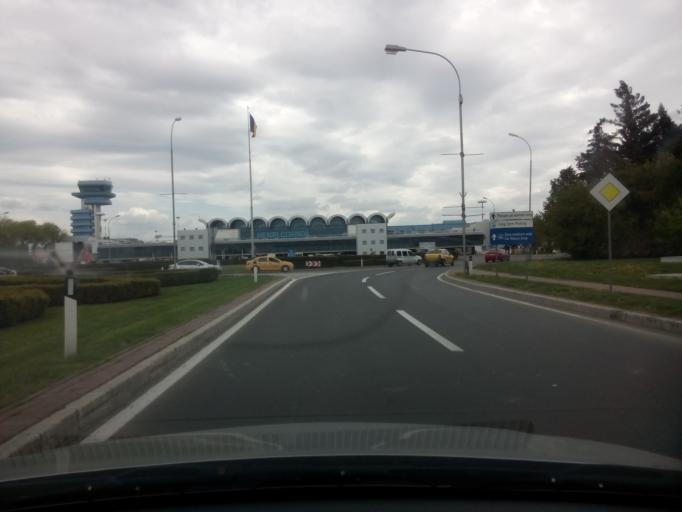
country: RO
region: Ilfov
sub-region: Comuna Otopeni
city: Otopeni
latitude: 44.5690
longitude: 26.0741
